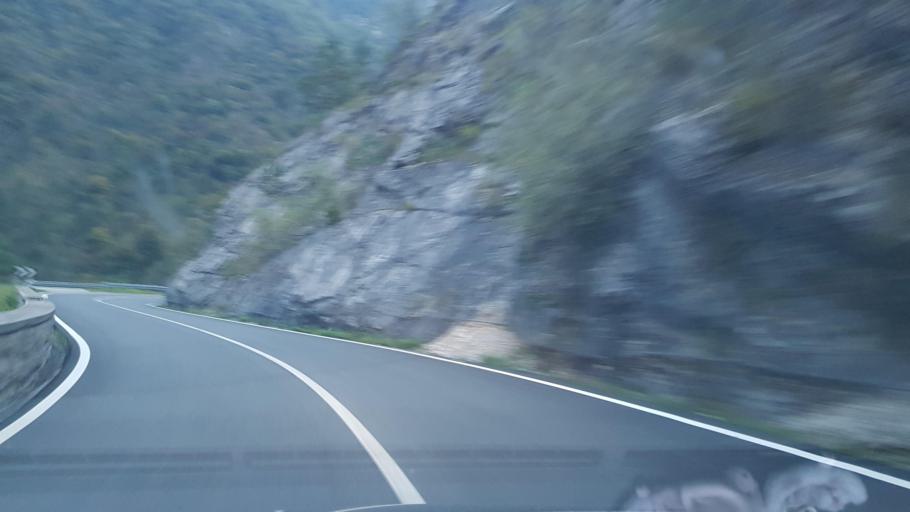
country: IT
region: Friuli Venezia Giulia
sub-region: Provincia di Pordenone
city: Anduins
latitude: 46.2557
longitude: 12.9746
